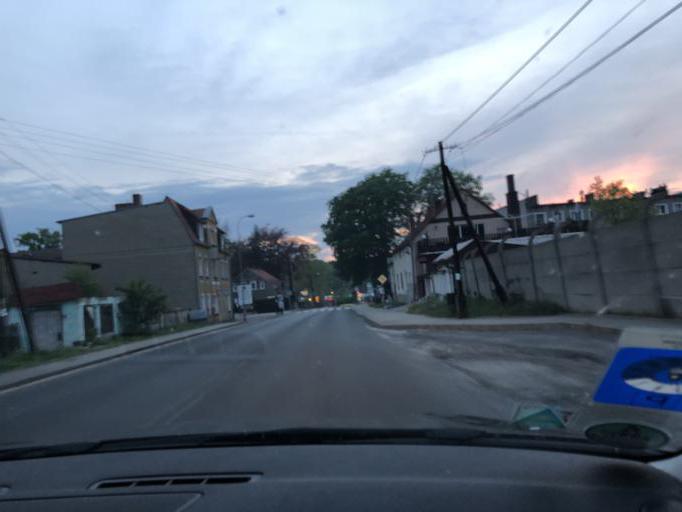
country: PL
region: Lubusz
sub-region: Powiat zarski
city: Leknica
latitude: 51.5414
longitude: 14.7371
